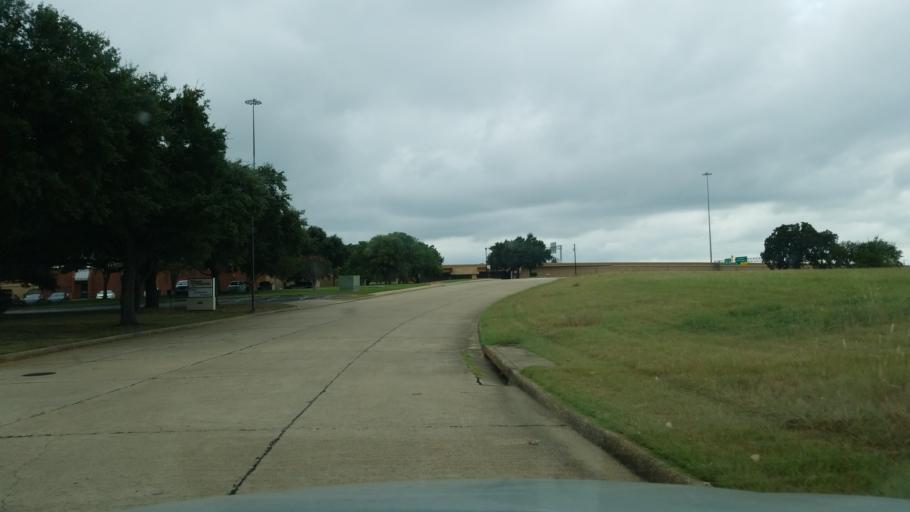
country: US
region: Texas
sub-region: Tarrant County
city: Bedford
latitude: 32.8400
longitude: -97.1127
